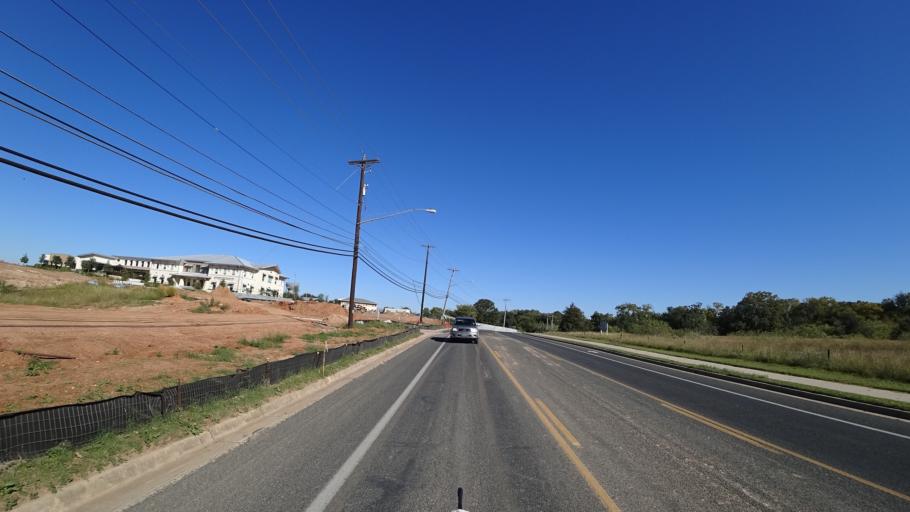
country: US
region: Texas
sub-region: Travis County
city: Austin
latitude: 30.2936
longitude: -97.6894
